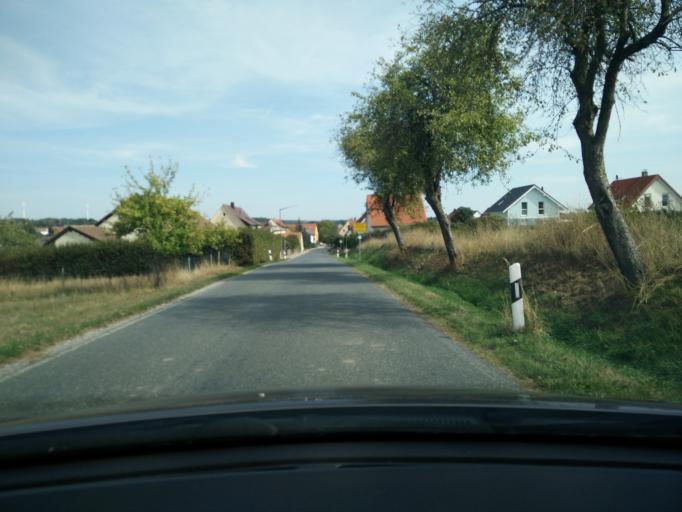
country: DE
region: Bavaria
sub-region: Regierungsbezirk Mittelfranken
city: Emskirchen
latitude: 49.5710
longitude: 10.7020
